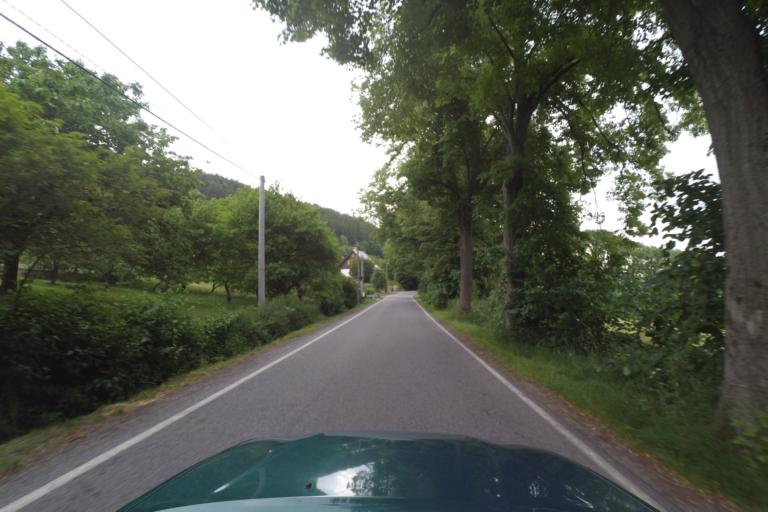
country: CZ
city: Cesky Dub
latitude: 50.7148
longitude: 14.9799
